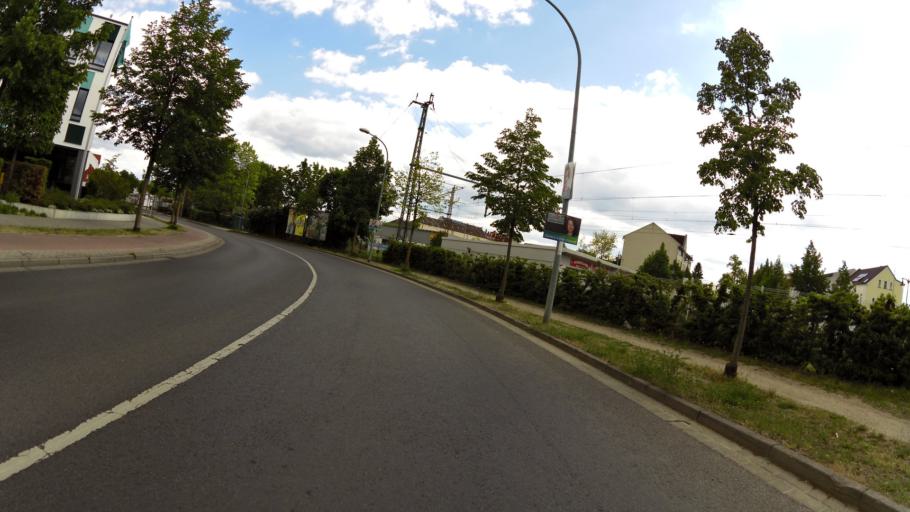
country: DE
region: Brandenburg
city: Furstenwalde
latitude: 52.3667
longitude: 14.0610
